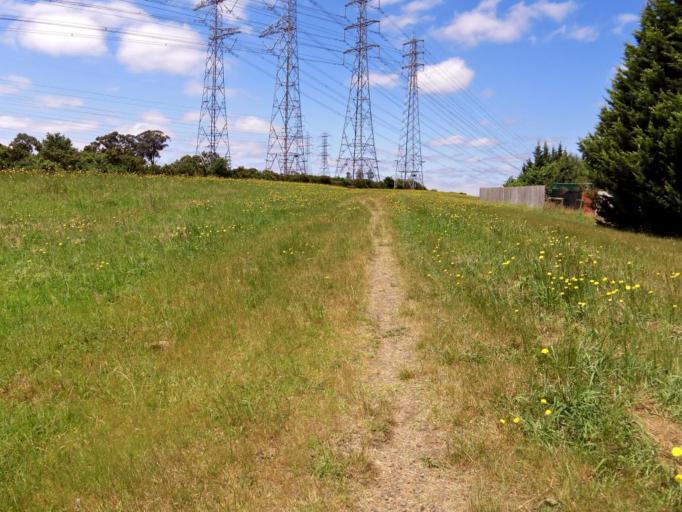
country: AU
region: Victoria
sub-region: Casey
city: Endeavour Hills
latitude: -37.9738
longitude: 145.2866
